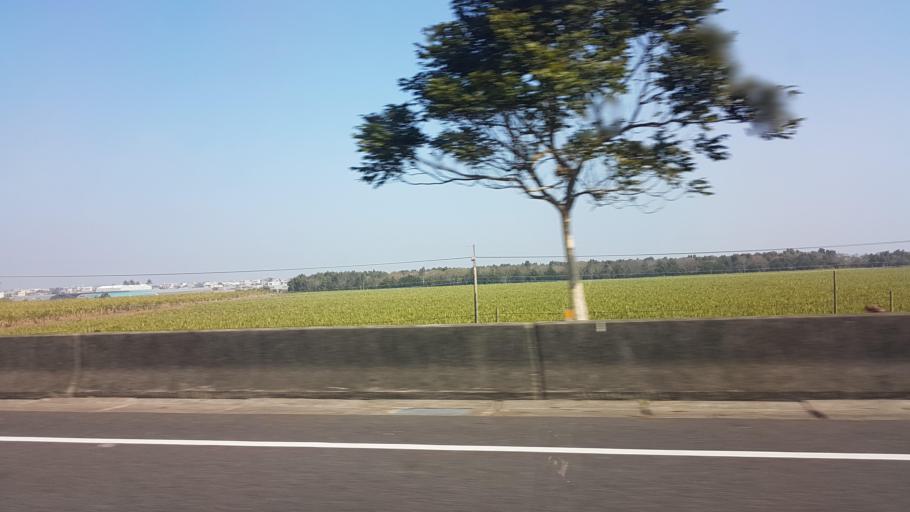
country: TW
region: Taiwan
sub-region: Chiayi
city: Taibao
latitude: 23.4262
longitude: 120.3497
